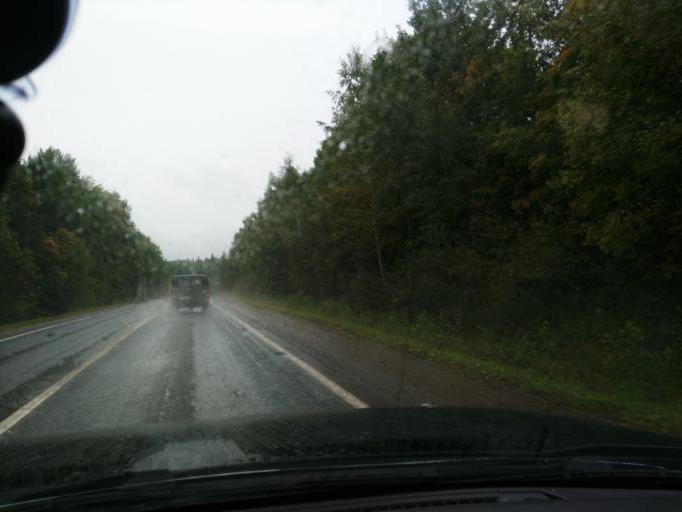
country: RU
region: Perm
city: Yugo-Kamskiy
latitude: 57.6264
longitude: 55.6174
